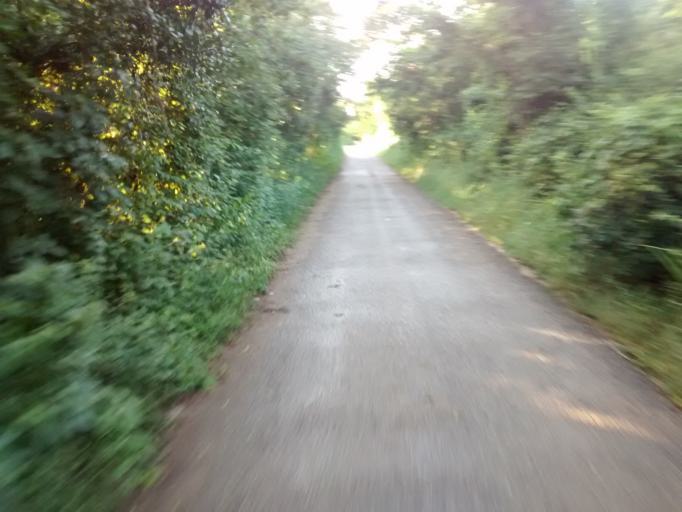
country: MX
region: Yucatan
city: Valladolid
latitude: 20.7252
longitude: -88.2295
